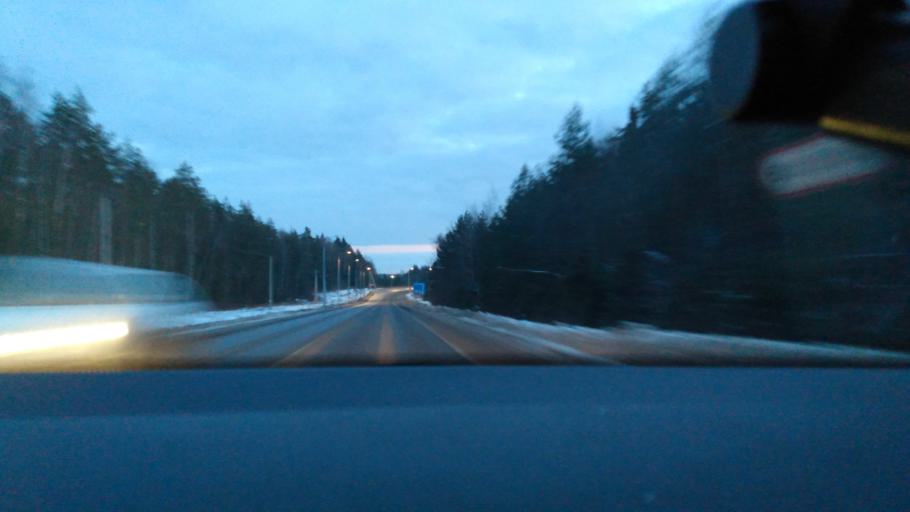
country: RU
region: Moskovskaya
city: Yegor'yevsk
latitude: 55.3120
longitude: 39.0760
